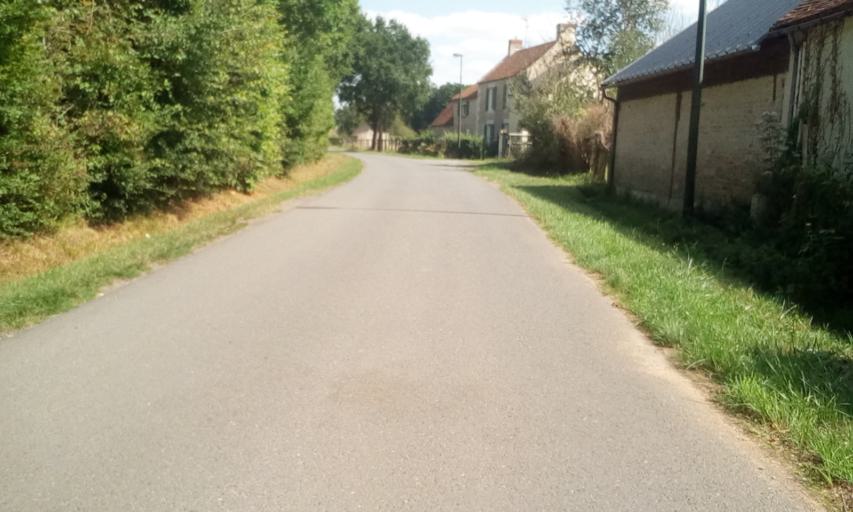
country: FR
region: Lower Normandy
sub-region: Departement du Calvados
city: Argences
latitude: 49.1320
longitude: -0.1298
